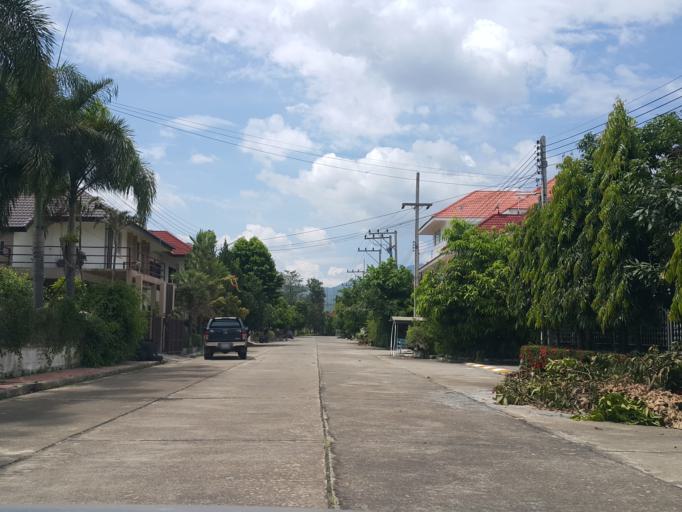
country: TH
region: Chiang Mai
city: Hang Dong
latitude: 18.7379
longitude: 98.9428
